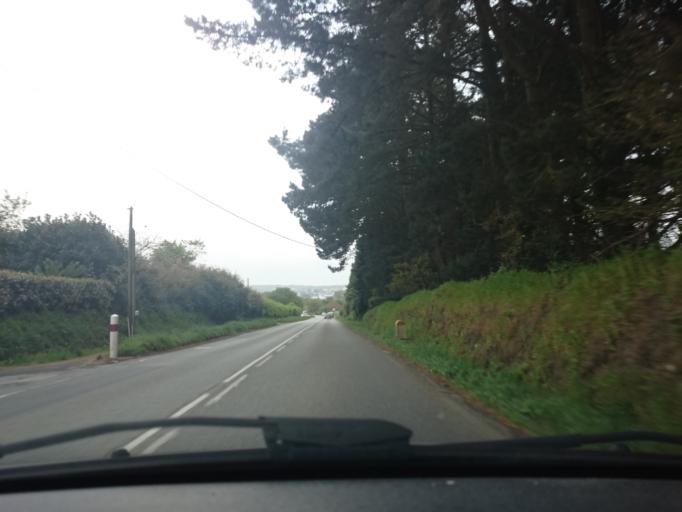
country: FR
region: Brittany
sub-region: Departement du Finistere
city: Saint-Renan
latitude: 48.4467
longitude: -4.6227
